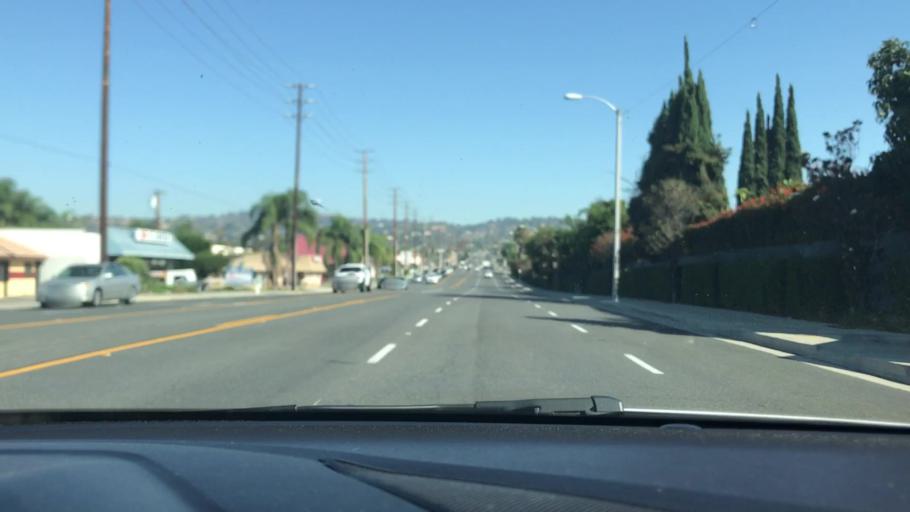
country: US
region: California
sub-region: Orange County
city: La Habra
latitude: 33.9284
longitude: -117.9330
